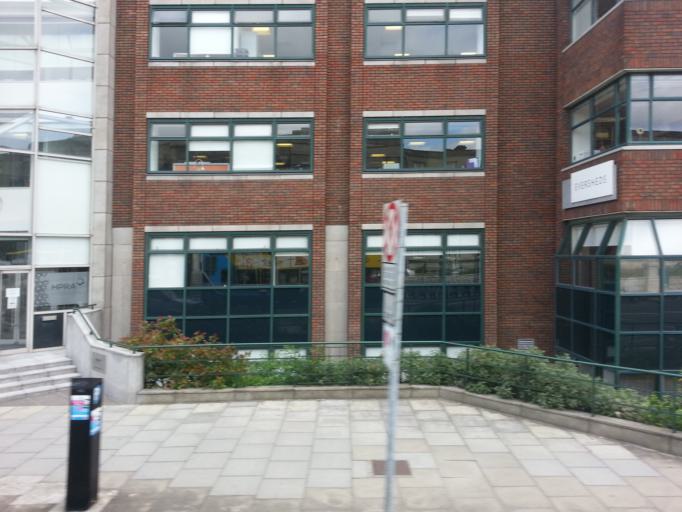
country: IE
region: Leinster
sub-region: Dublin City
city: Dublin
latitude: 53.3344
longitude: -6.2583
